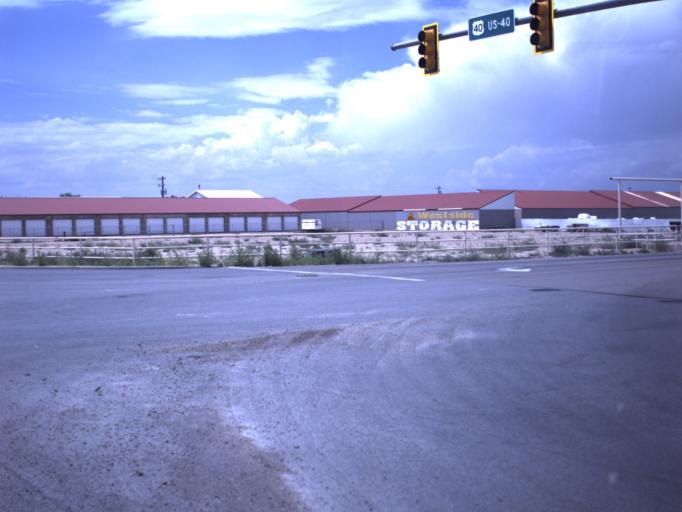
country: US
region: Utah
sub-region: Duchesne County
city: Roosevelt
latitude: 40.2742
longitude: -110.0288
